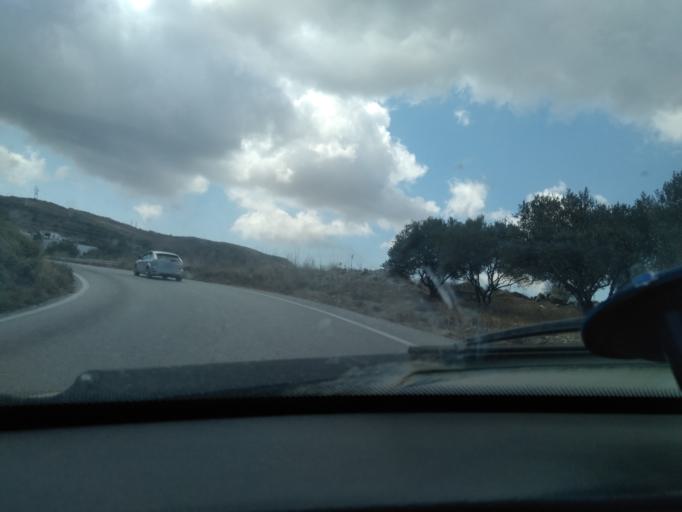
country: GR
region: Crete
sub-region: Nomos Lasithiou
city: Makry-Gialos
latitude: 35.0954
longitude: 26.0706
